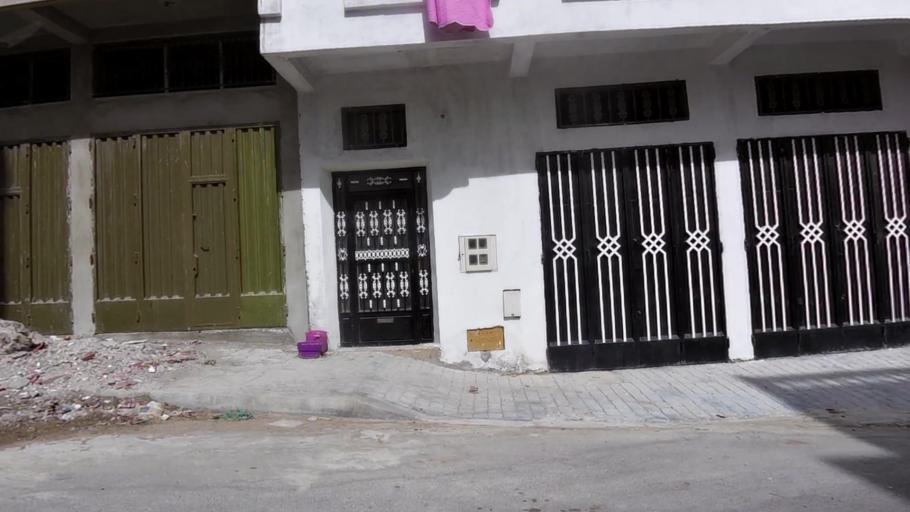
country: MA
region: Tanger-Tetouan
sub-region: Tanger-Assilah
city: Tangier
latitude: 35.7638
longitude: -5.7625
